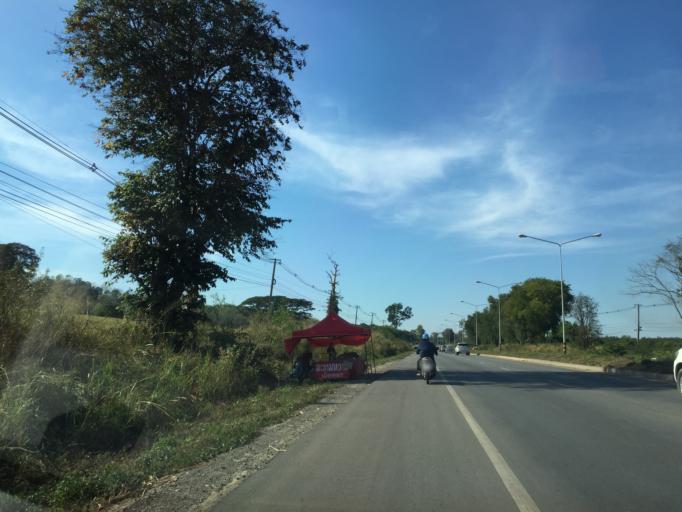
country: TH
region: Loei
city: Wang Saphung
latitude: 17.2953
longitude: 101.8164
